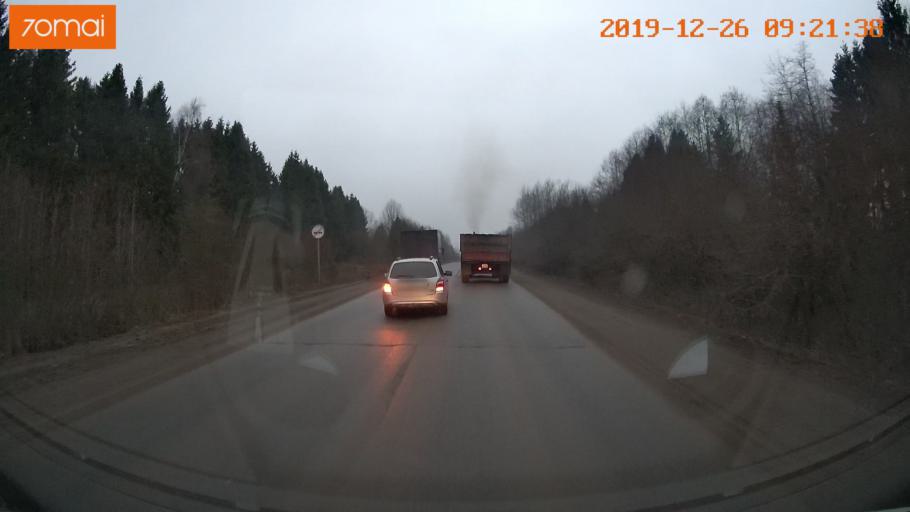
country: RU
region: Vologda
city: Gryazovets
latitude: 58.9713
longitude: 40.2236
